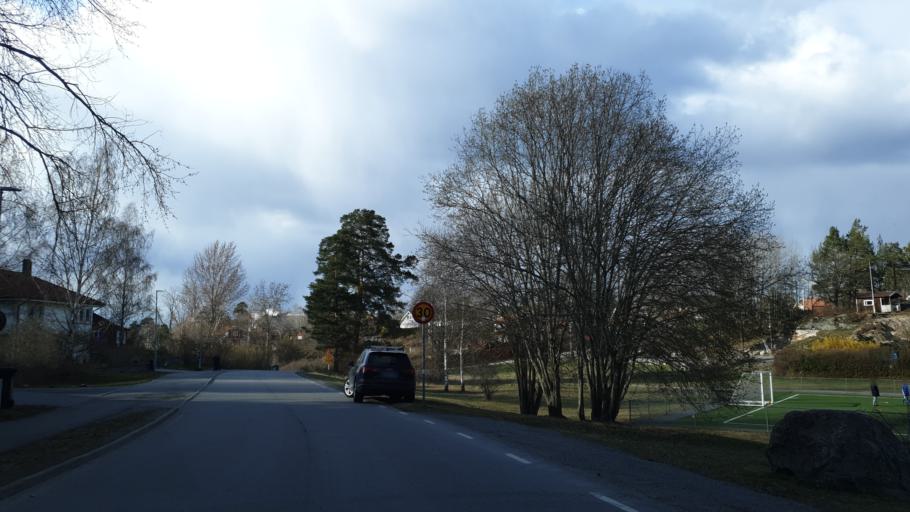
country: SE
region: Stockholm
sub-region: Lidingo
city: Lidingoe
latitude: 59.3879
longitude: 18.1199
